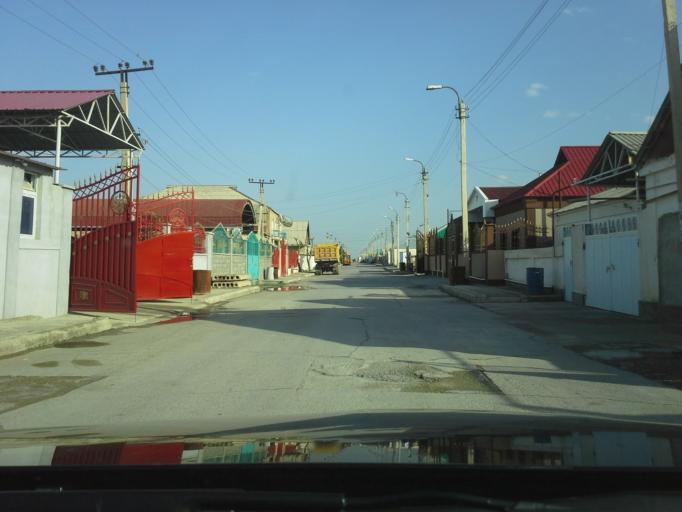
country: TM
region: Ahal
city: Abadan
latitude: 38.0191
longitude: 58.2290
